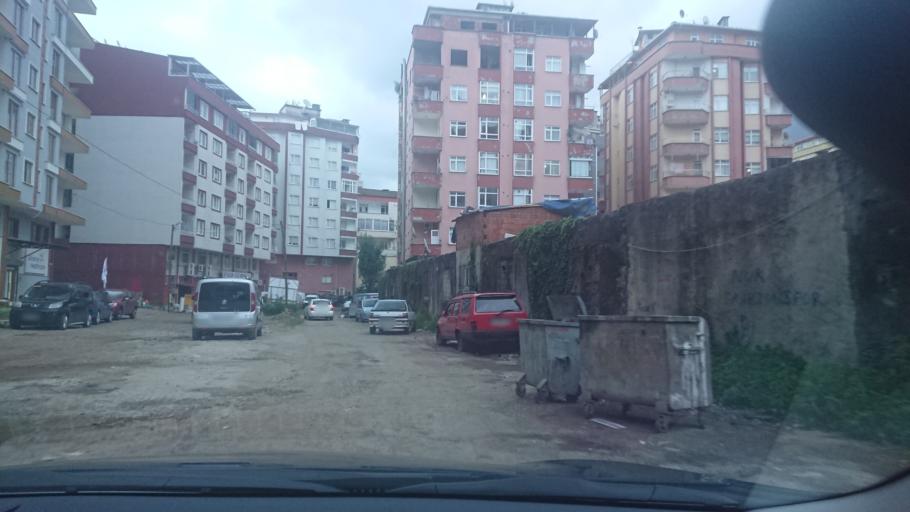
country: TR
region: Rize
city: Rize
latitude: 41.0270
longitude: 40.5129
